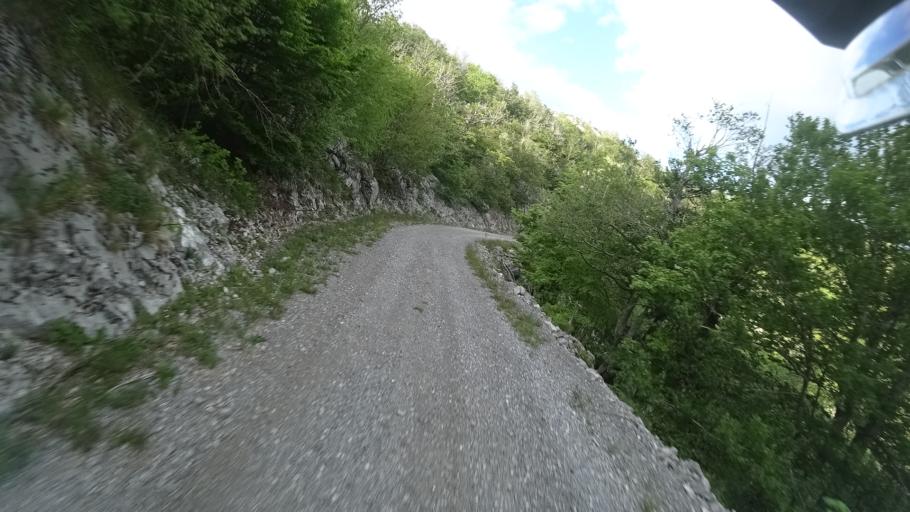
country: HR
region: Licko-Senjska
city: Gospic
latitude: 44.4564
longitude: 15.3026
